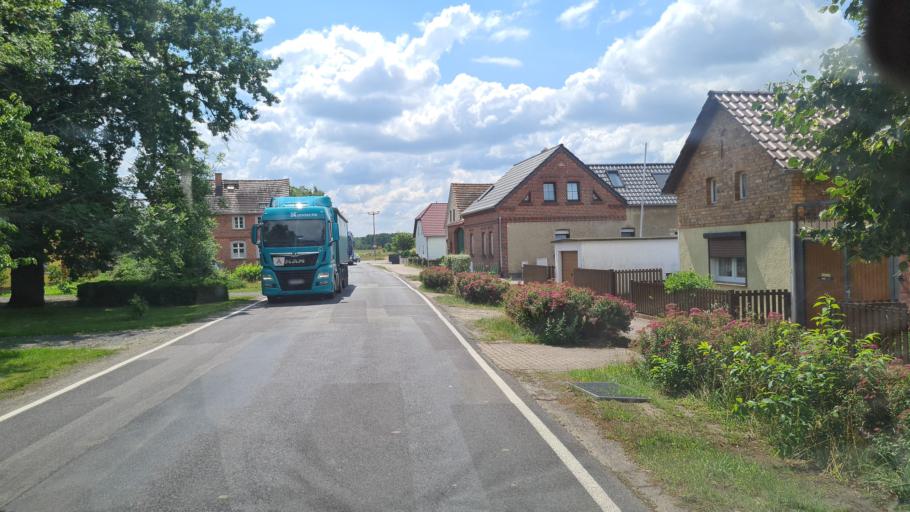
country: DE
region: Brandenburg
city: Welzow
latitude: 51.4927
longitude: 14.1219
